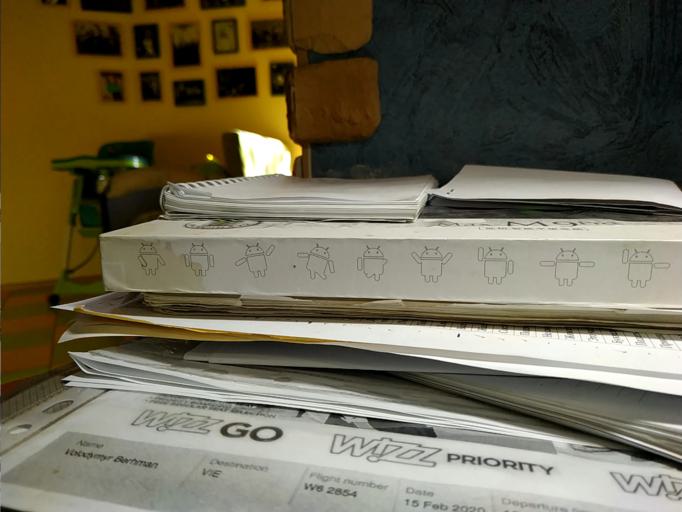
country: RU
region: Novgorod
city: Kholm
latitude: 57.2646
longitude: 31.2737
